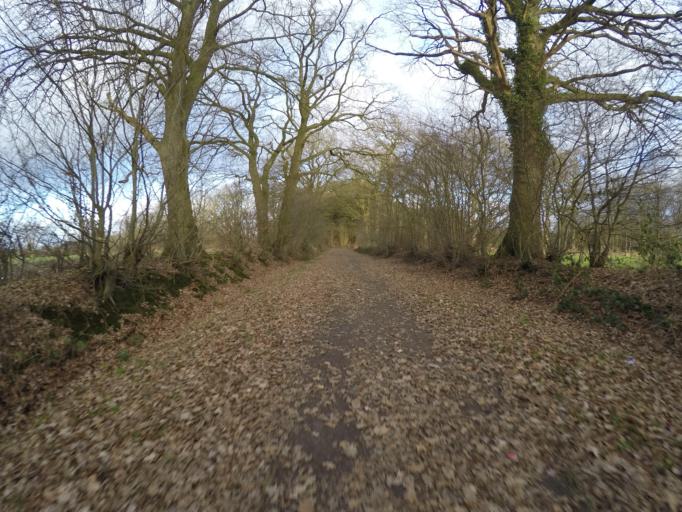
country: DE
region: Schleswig-Holstein
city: Quickborn
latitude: 53.7208
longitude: 9.8939
